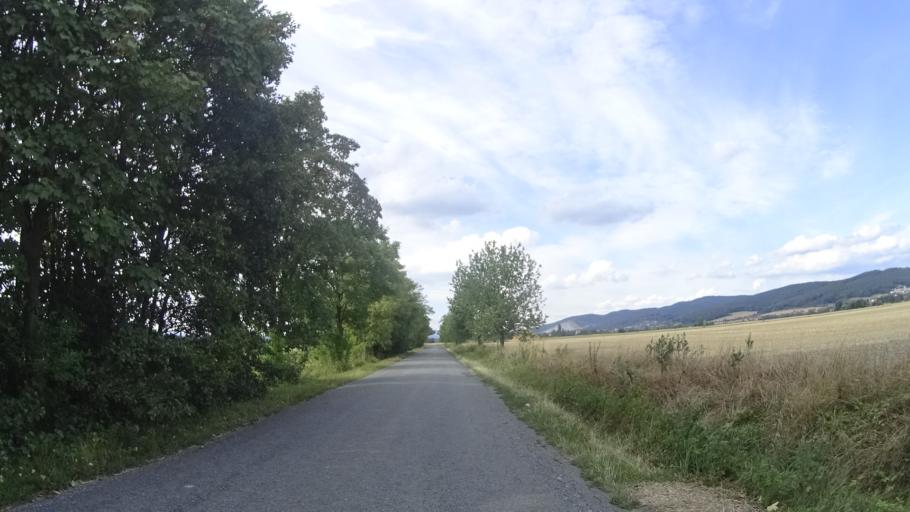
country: CZ
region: Olomoucky
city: Dubicko
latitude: 49.8139
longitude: 16.9427
